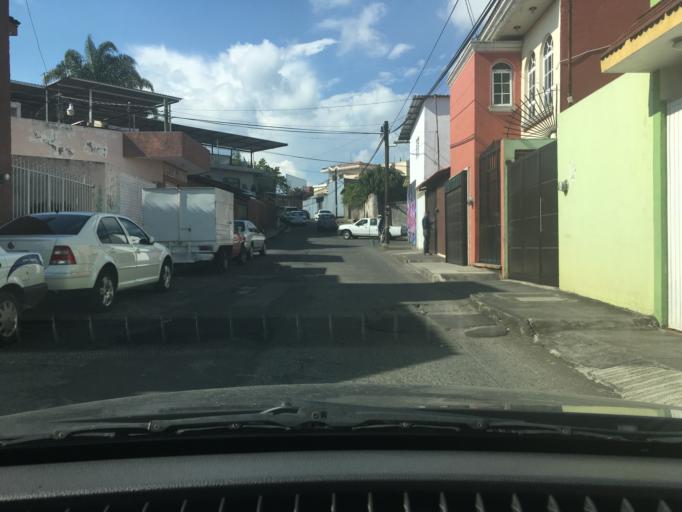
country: MX
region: Michoacan
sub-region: Uruapan
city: Uruapan
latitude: 19.4095
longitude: -102.0645
